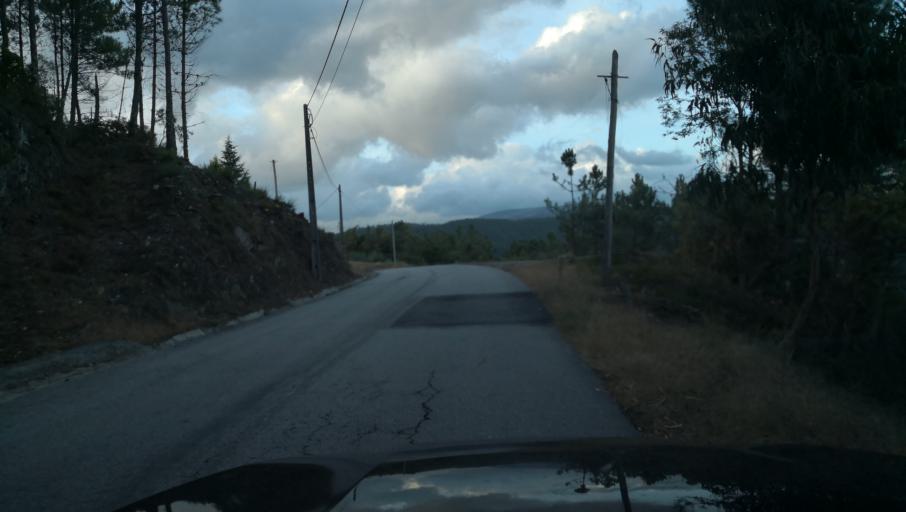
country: PT
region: Vila Real
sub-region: Santa Marta de Penaguiao
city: Santa Marta de Penaguiao
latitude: 41.2534
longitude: -7.8472
